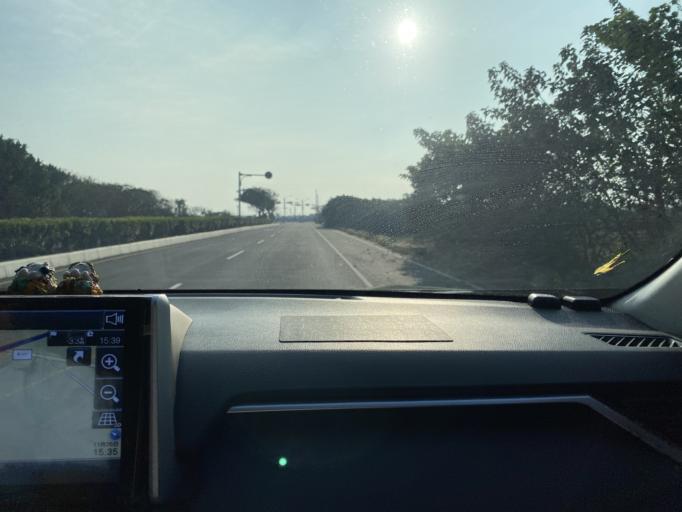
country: TW
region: Taiwan
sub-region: Changhua
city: Chang-hua
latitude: 23.9613
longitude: 120.3714
